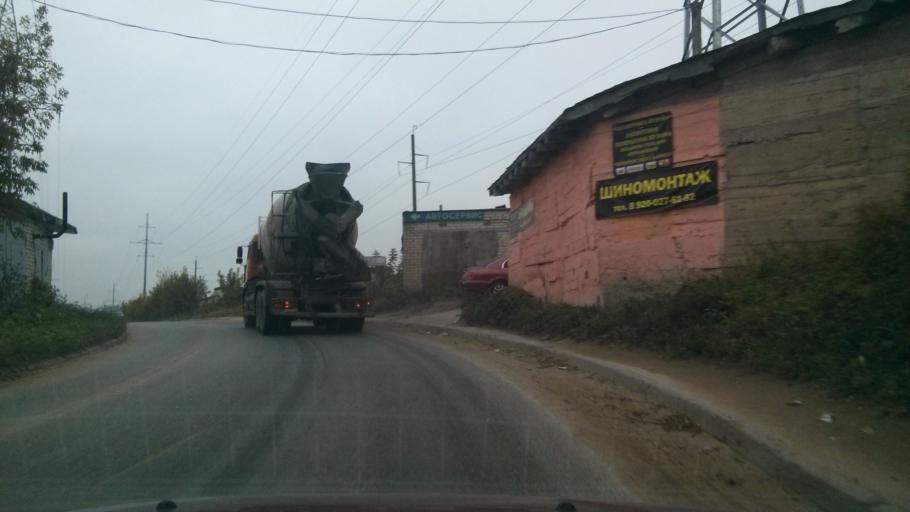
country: RU
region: Nizjnij Novgorod
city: Nizhniy Novgorod
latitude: 56.3046
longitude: 44.0088
